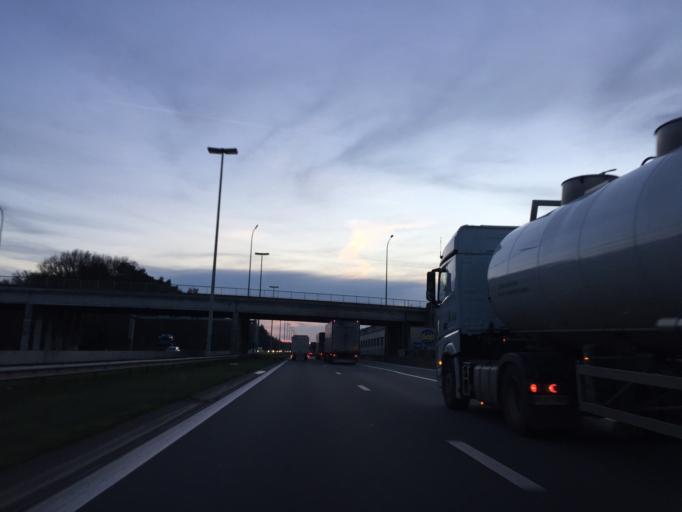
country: BE
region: Flanders
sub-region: Provincie Antwerpen
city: Brasschaat
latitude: 51.2839
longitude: 4.5119
